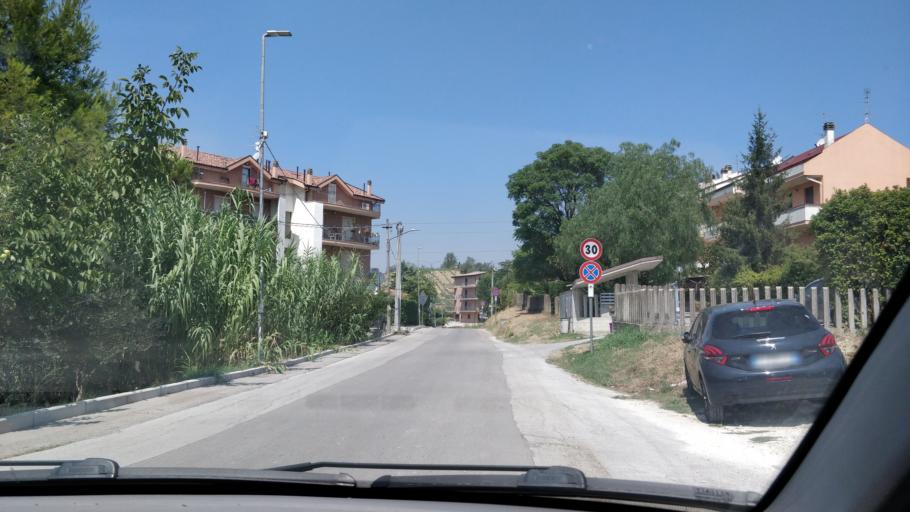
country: IT
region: Abruzzo
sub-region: Provincia di Chieti
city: Sambuceto
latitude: 42.3982
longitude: 14.1705
